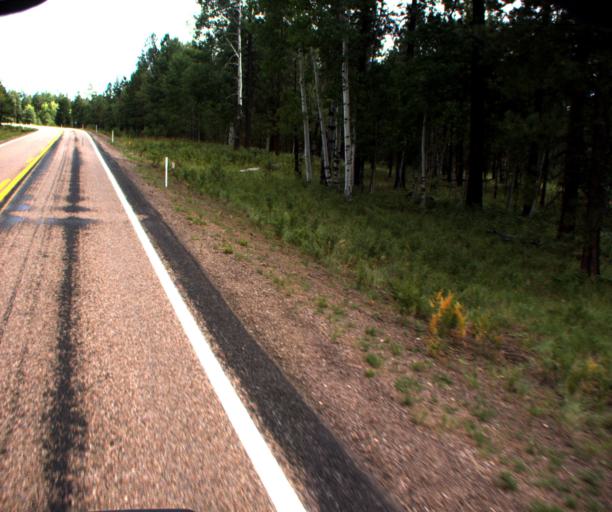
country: US
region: Arizona
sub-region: Navajo County
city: Pinetop-Lakeside
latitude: 34.0302
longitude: -109.6596
